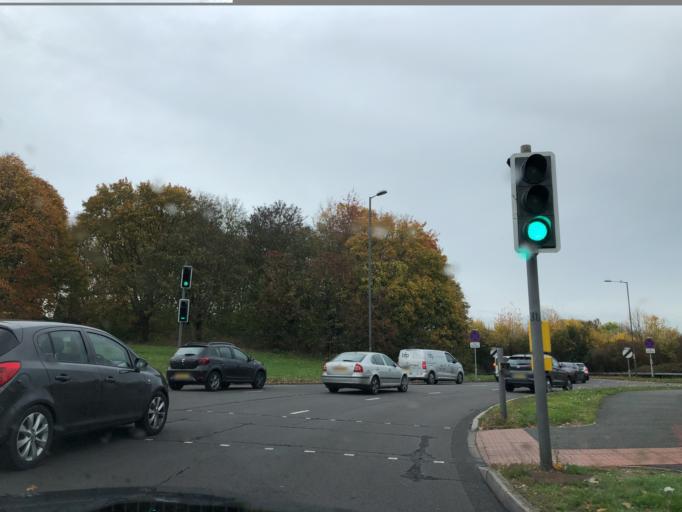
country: GB
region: England
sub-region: Hampshire
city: Basingstoke
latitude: 51.2767
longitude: -1.0761
